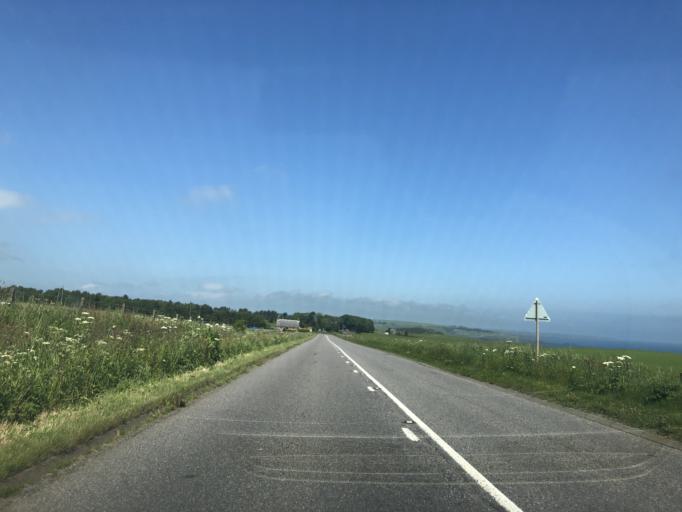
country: GB
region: Scotland
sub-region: Aberdeenshire
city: Stonehaven
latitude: 56.9375
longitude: -2.2068
